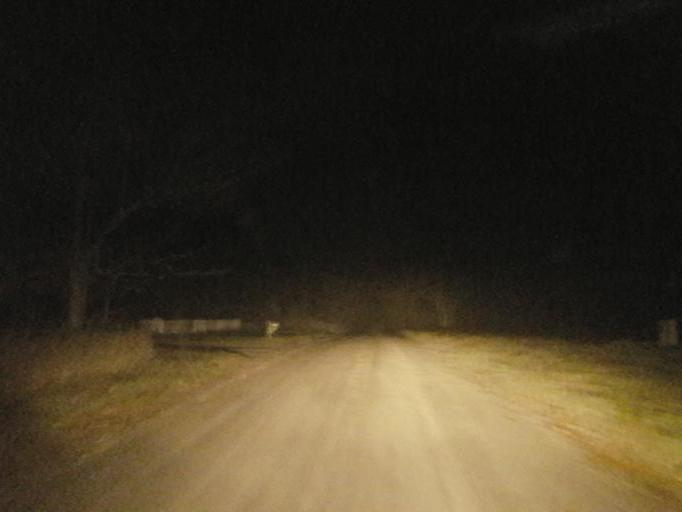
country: US
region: Michigan
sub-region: Isabella County
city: Lake Isabella
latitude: 43.5356
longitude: -85.0657
